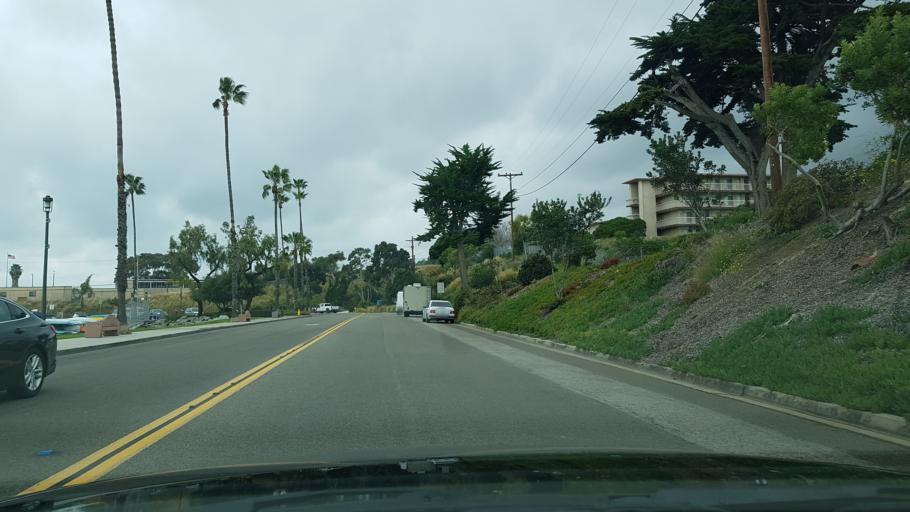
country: US
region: California
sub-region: San Diego County
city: Camp Pendleton South
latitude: 33.2130
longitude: -117.3943
